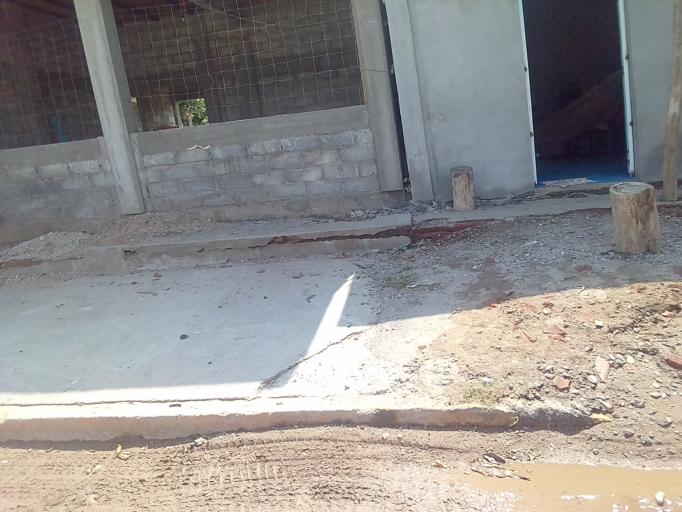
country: MX
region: Oaxaca
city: Union Hidalgo
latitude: 16.4712
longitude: -94.8357
